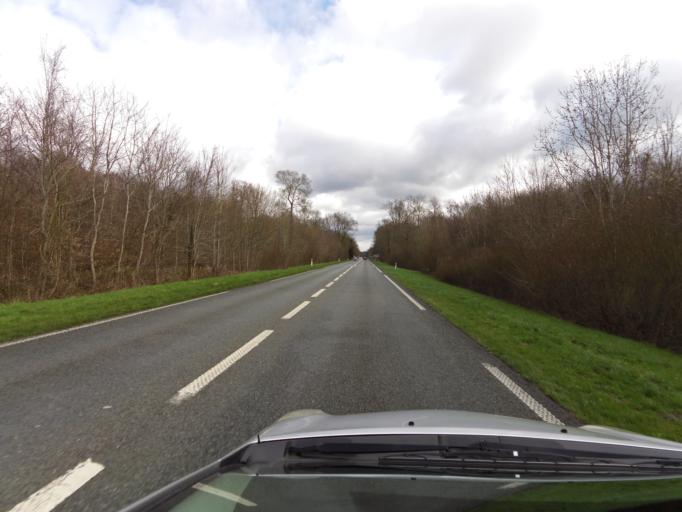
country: FR
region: Picardie
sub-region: Departement de l'Oise
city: Fleurines
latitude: 49.2803
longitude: 2.5971
